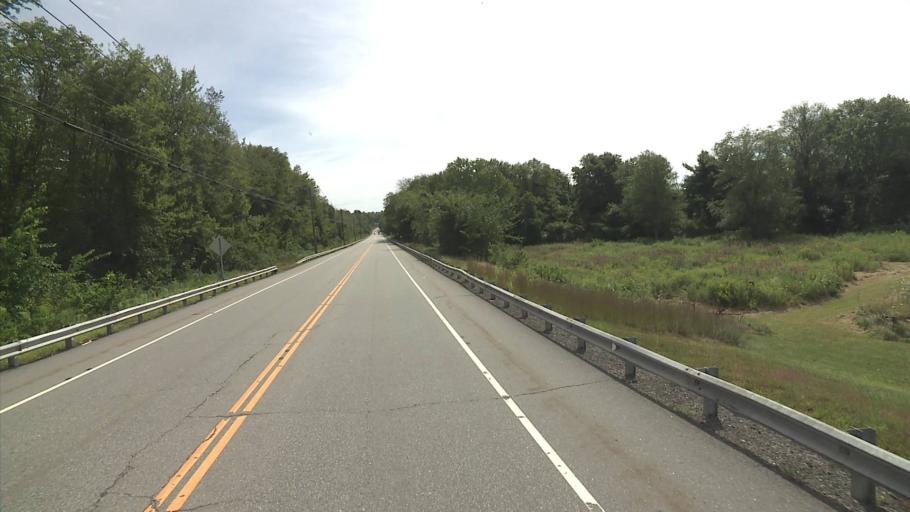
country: US
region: Connecticut
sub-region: Windham County
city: South Woodstock
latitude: 41.9342
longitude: -71.9442
